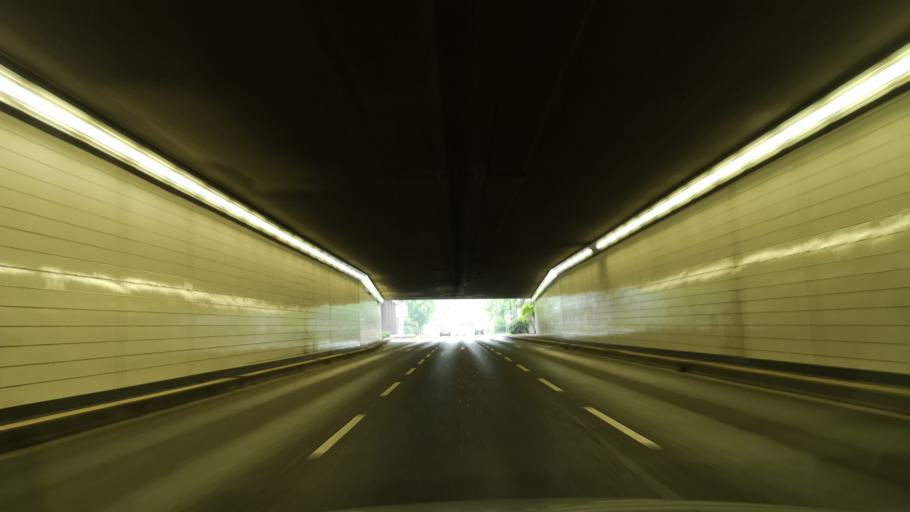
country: DE
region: North Rhine-Westphalia
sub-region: Regierungsbezirk Dusseldorf
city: Essen
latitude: 51.4522
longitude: 7.0173
